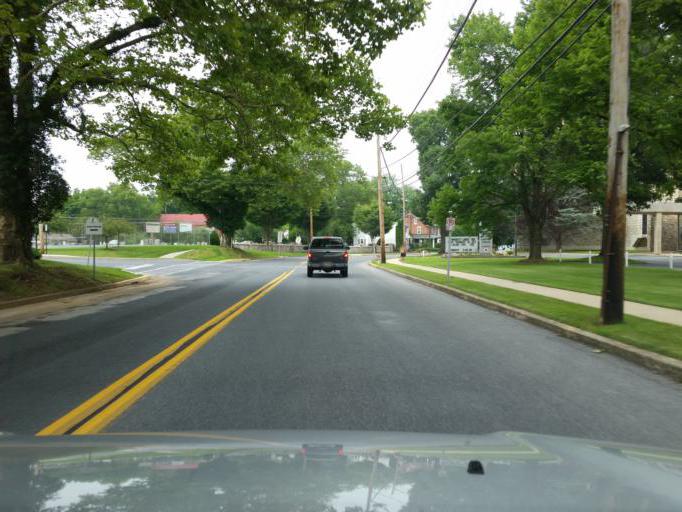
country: US
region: Pennsylvania
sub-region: Lancaster County
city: Lititz
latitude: 40.1549
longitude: -76.3125
